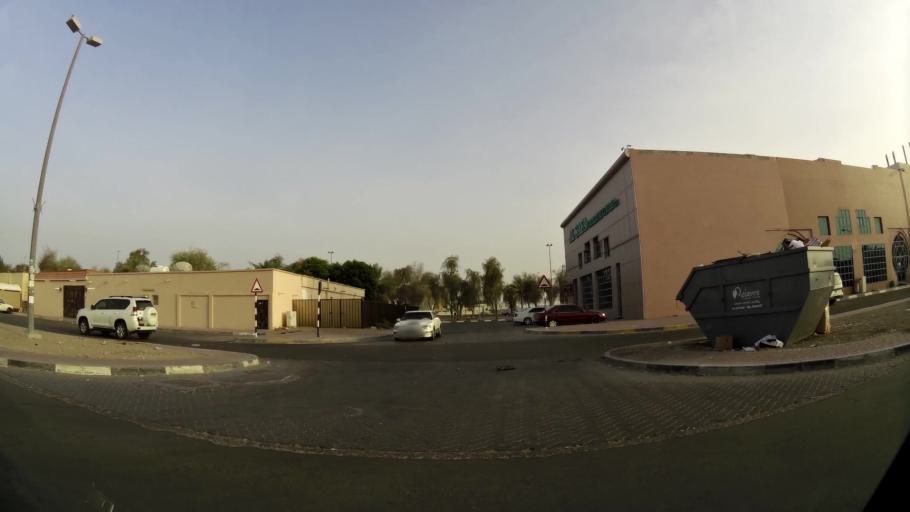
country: AE
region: Abu Dhabi
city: Al Ain
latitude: 24.2428
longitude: 55.7310
